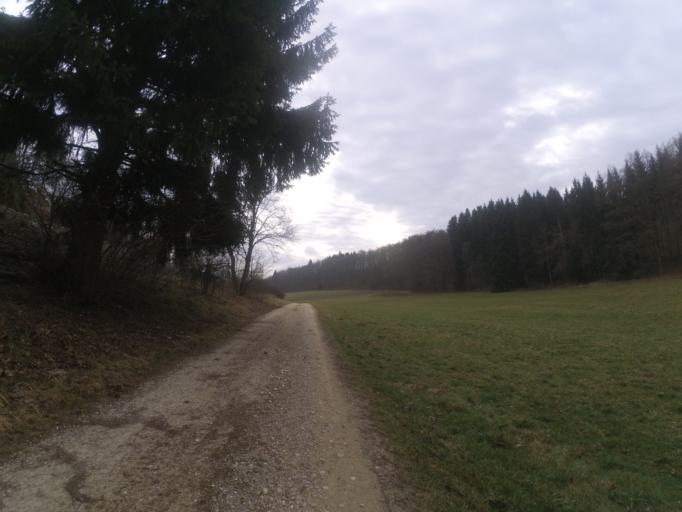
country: DE
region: Baden-Wuerttemberg
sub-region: Tuebingen Region
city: Mehrstetten
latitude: 48.3656
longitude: 9.5390
